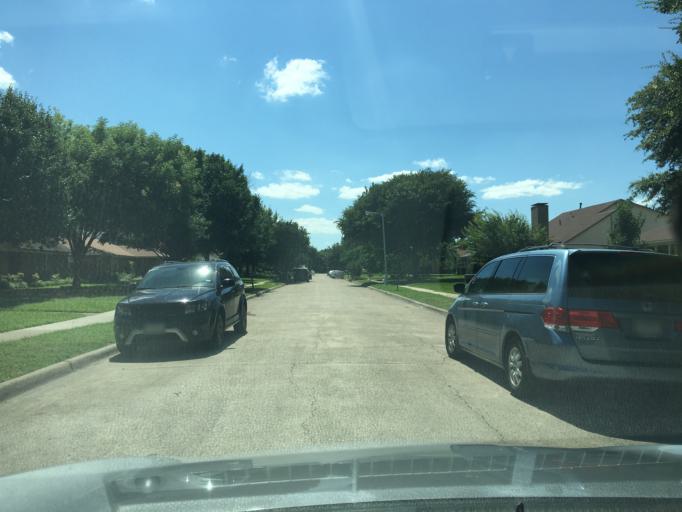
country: US
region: Texas
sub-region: Dallas County
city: Richardson
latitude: 32.9528
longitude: -96.7072
